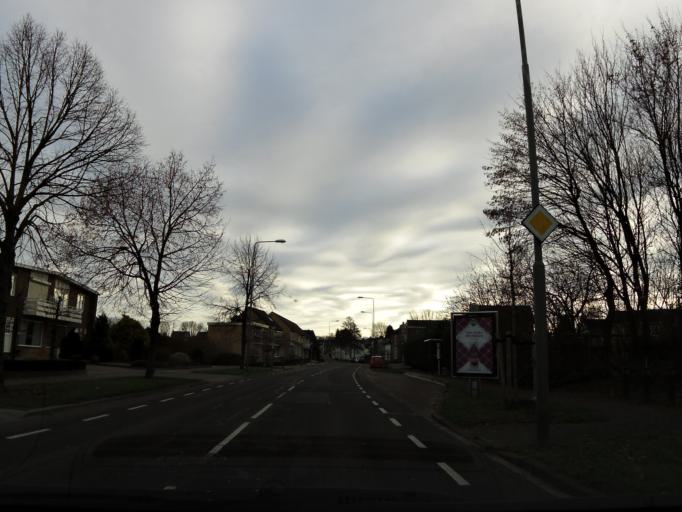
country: NL
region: Limburg
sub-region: Gemeente Schinnen
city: Puth
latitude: 50.9434
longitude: 5.8408
